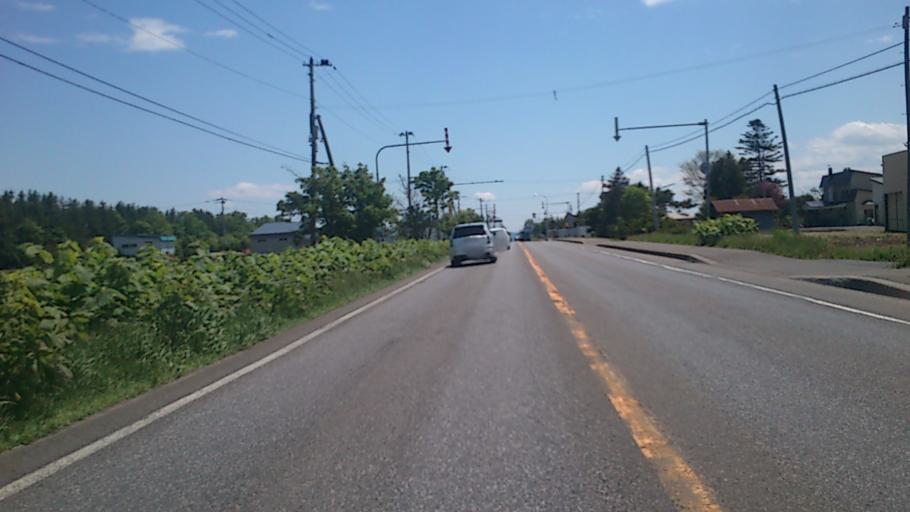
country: JP
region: Hokkaido
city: Nayoro
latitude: 44.2481
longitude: 142.3948
